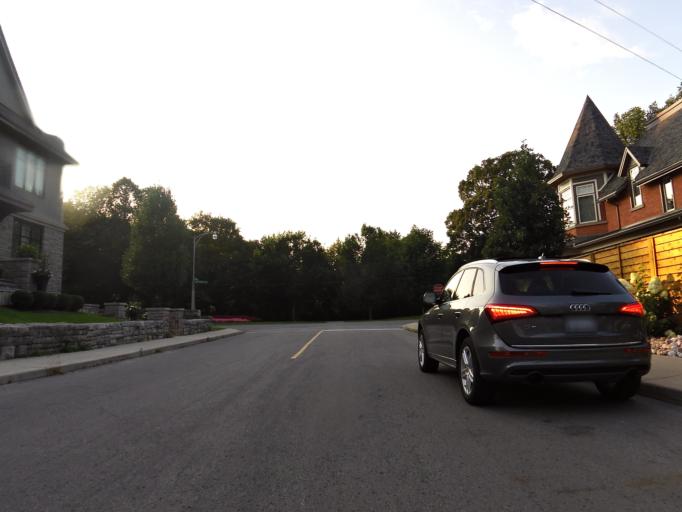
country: CA
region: Ontario
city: Ottawa
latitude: 45.3939
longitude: -75.6897
